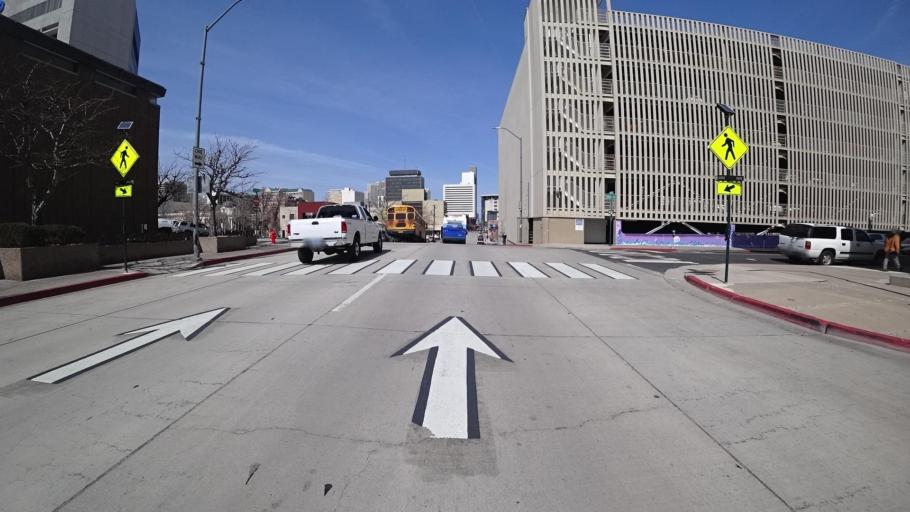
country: US
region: Nevada
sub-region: Washoe County
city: Reno
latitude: 39.5227
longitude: -119.8101
